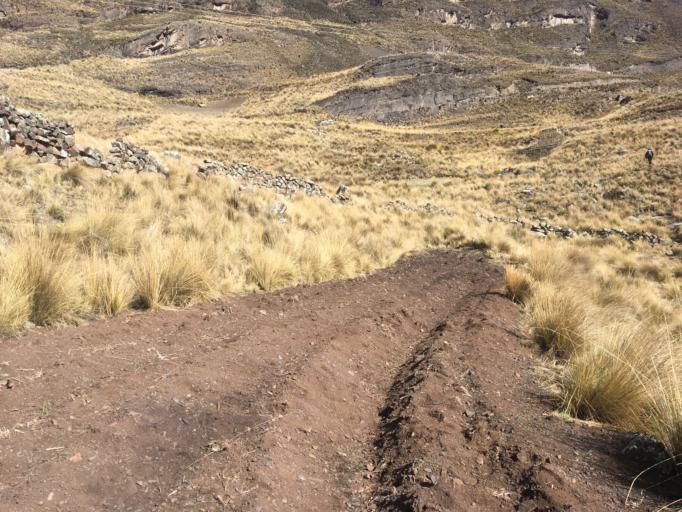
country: BO
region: La Paz
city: La Paz
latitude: -16.4036
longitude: -68.0158
